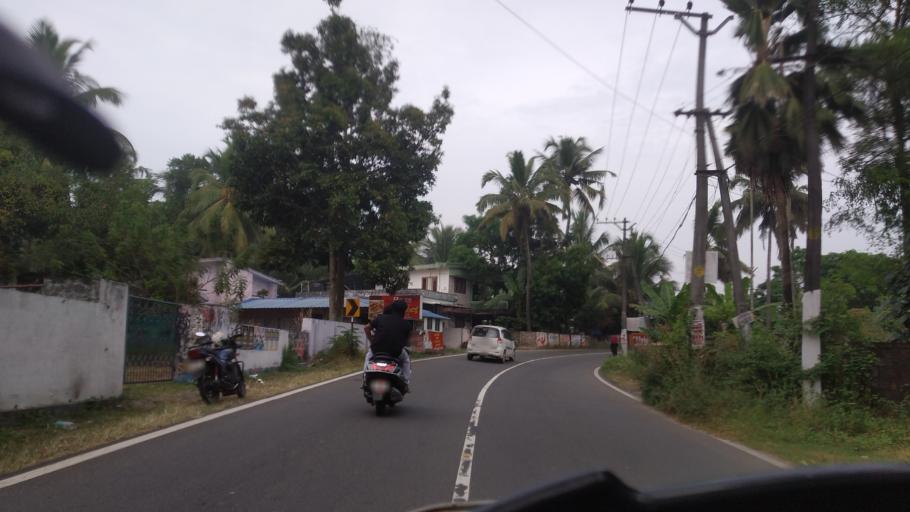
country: IN
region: Kerala
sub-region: Ernakulam
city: Elur
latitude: 10.1504
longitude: 76.2640
